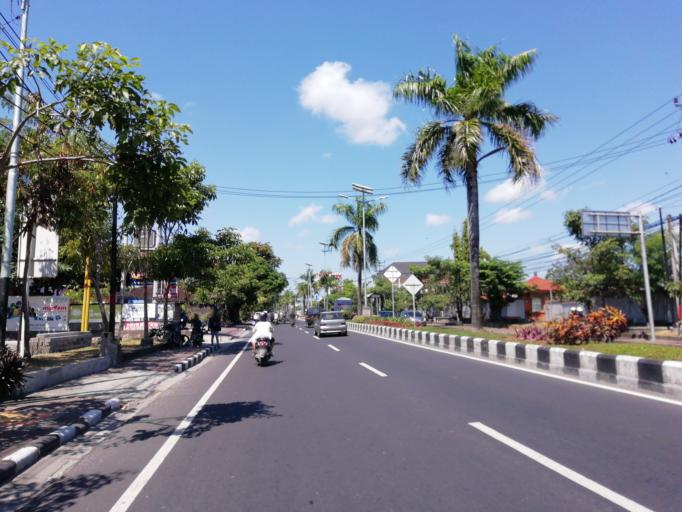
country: ID
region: Bali
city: Kelanabian
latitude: -8.7630
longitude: 115.1788
